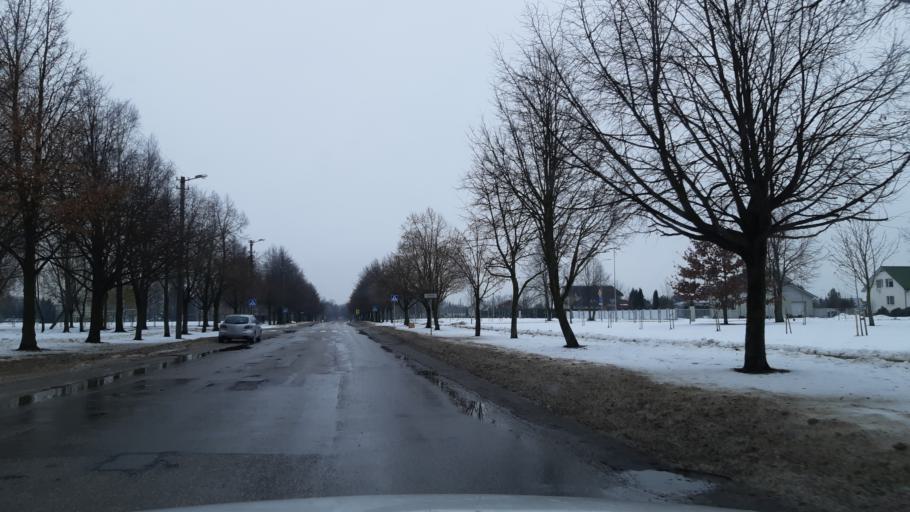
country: LT
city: Vilkaviskis
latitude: 54.6560
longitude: 23.0287
